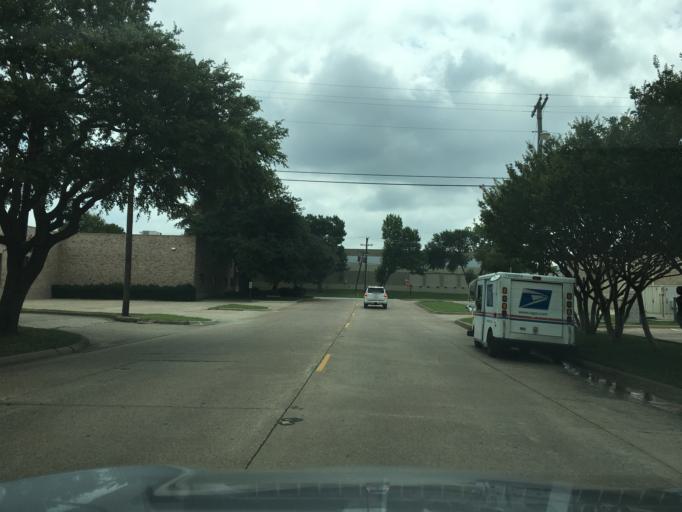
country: US
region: Texas
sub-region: Dallas County
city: Addison
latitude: 32.9371
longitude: -96.8321
